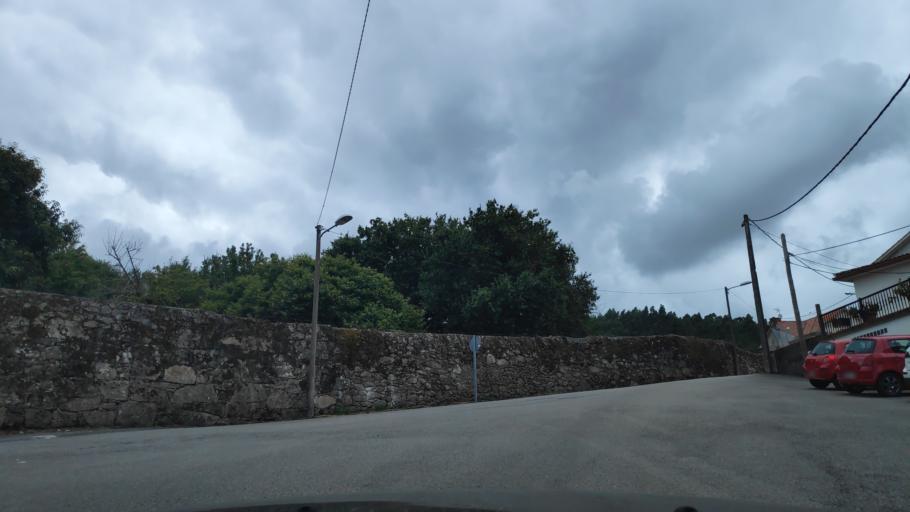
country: ES
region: Galicia
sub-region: Provincia da Coruna
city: Padron
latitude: 42.7335
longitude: -8.6651
